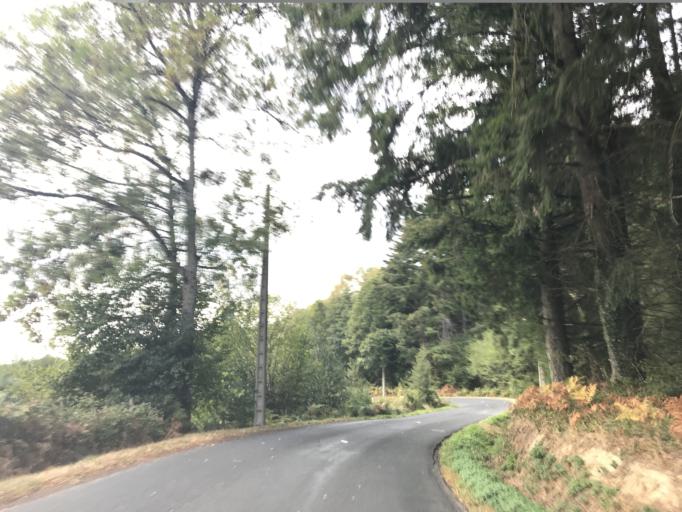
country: FR
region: Auvergne
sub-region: Departement du Puy-de-Dome
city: Celles-sur-Durolle
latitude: 45.7839
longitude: 3.6292
